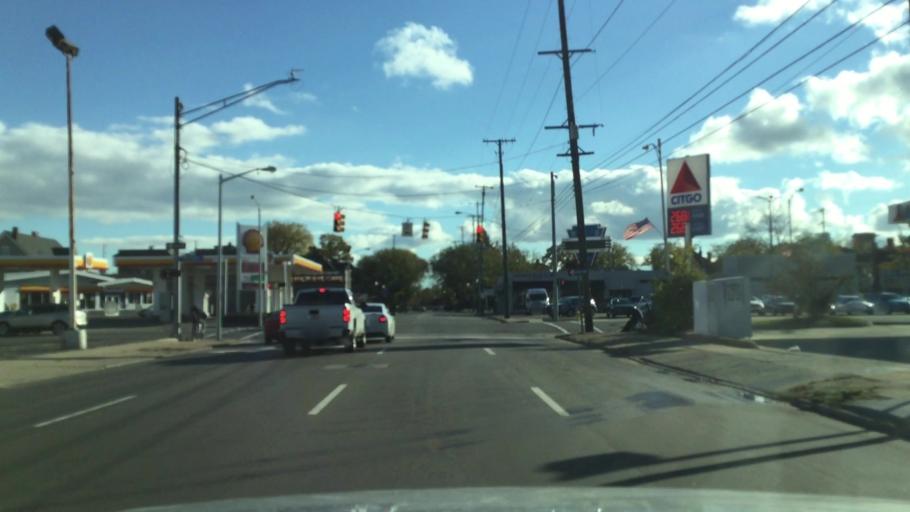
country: US
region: Michigan
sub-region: Kalamazoo County
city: Kalamazoo
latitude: 42.2920
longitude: -85.5898
